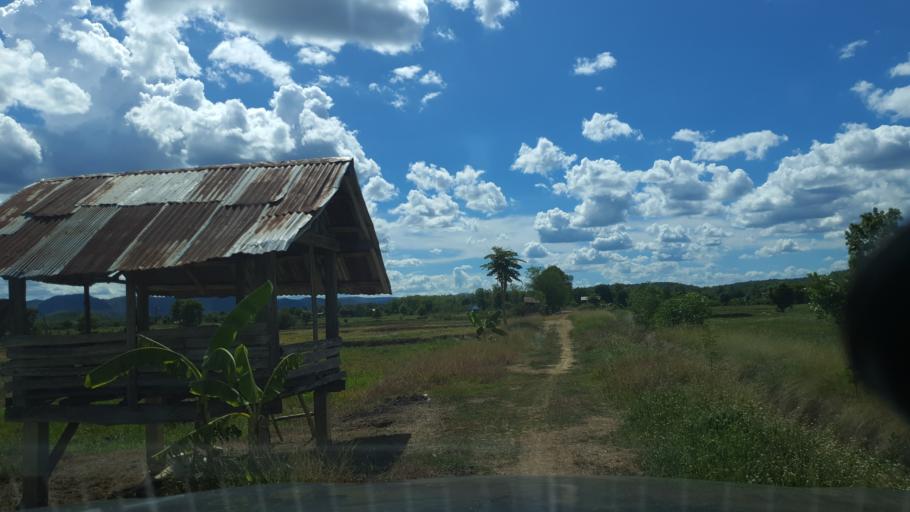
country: TH
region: Sukhothai
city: Thung Saliam
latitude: 17.3376
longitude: 99.4430
